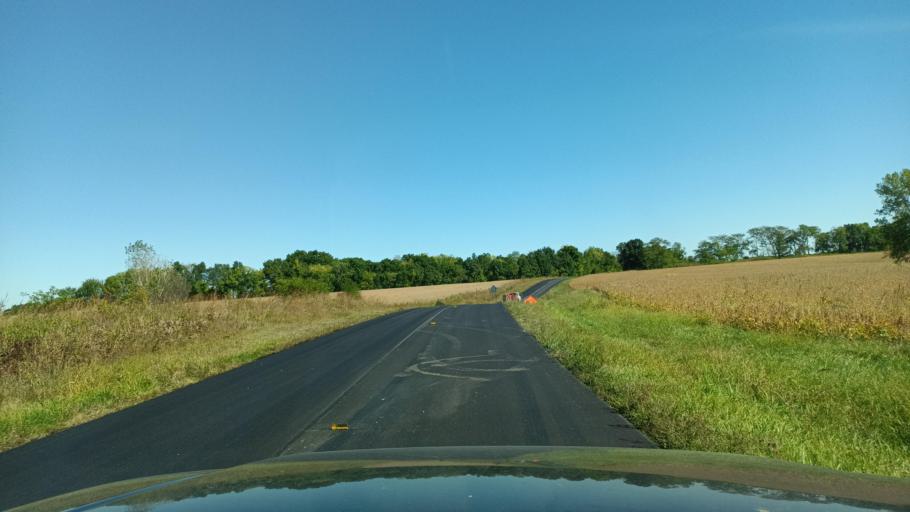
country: US
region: Missouri
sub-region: Macon County
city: La Plata
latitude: 39.9268
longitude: -92.5401
